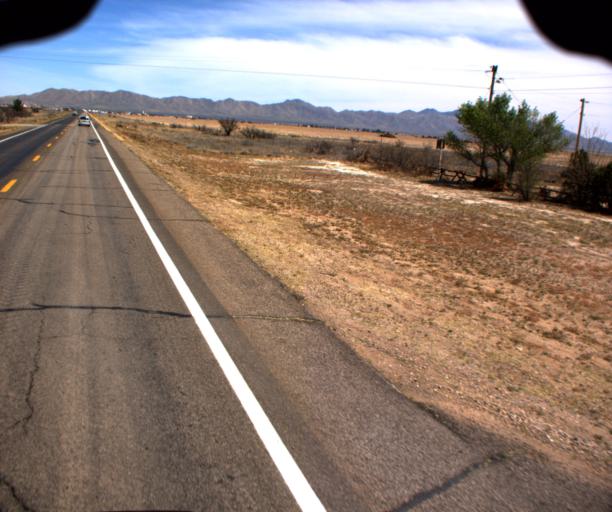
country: US
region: Arizona
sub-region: Cochise County
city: Willcox
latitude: 32.2304
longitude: -109.8591
